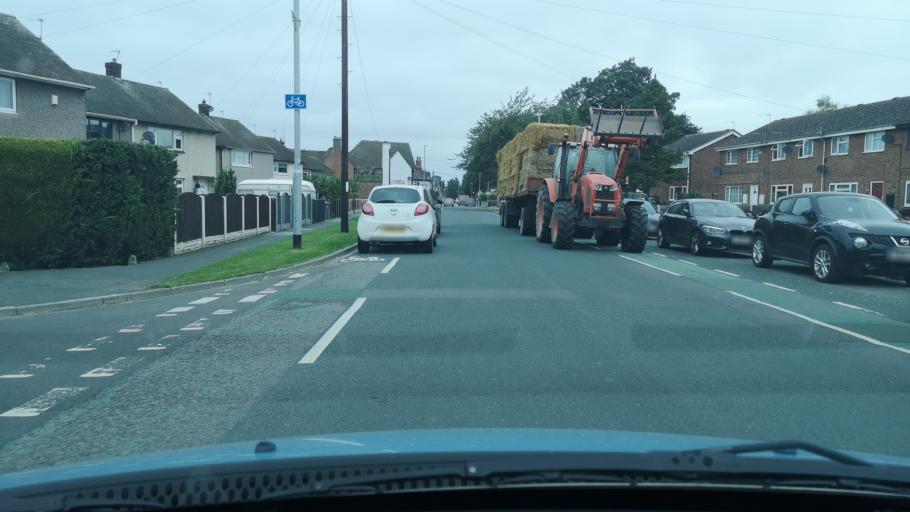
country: GB
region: England
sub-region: East Riding of Yorkshire
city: Goole
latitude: 53.6925
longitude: -0.8660
